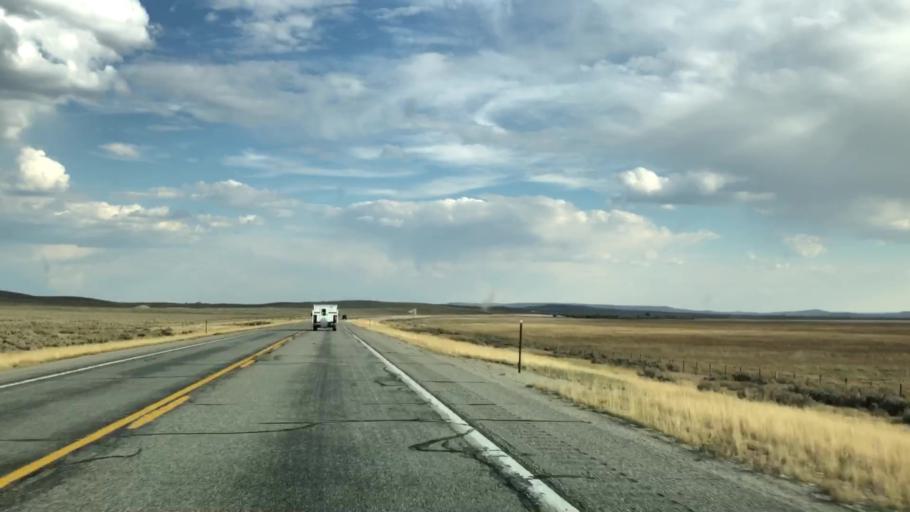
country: US
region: Wyoming
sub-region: Sublette County
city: Pinedale
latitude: 43.0361
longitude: -110.1334
